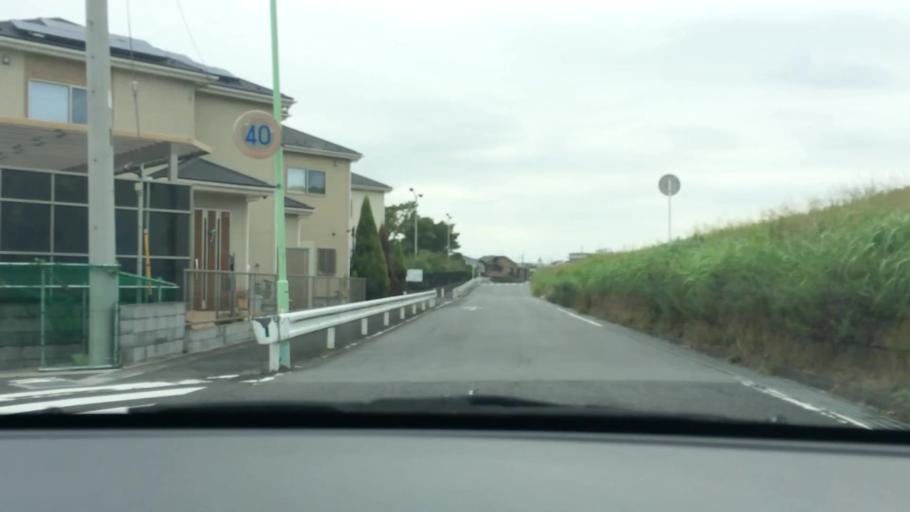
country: JP
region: Chiba
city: Matsudo
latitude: 35.8044
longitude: 139.8866
